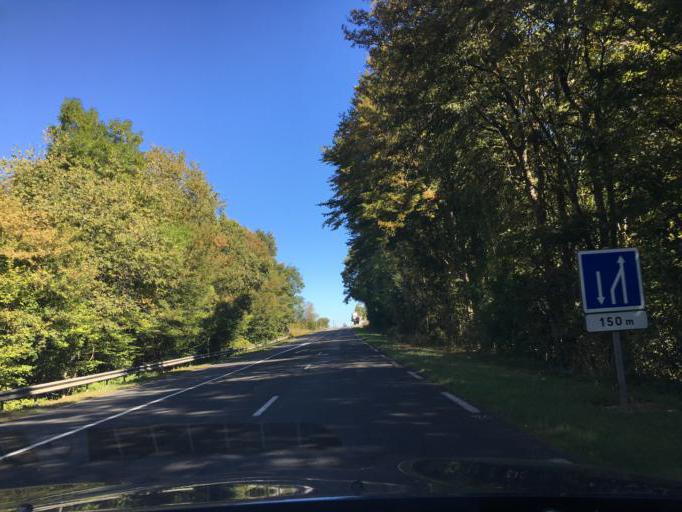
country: FR
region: Centre
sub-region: Departement d'Indre-et-Loire
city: Azay-le-Rideau
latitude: 47.2464
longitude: 0.4411
